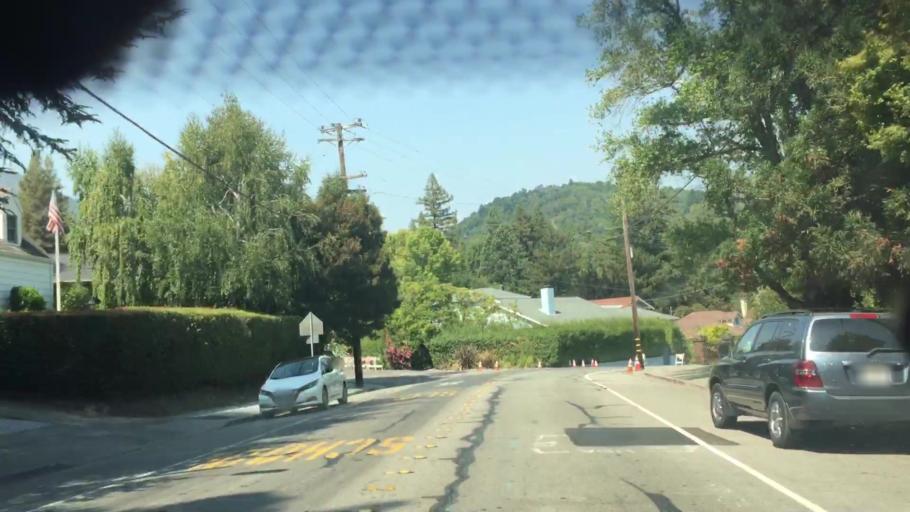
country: US
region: California
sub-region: Marin County
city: Larkspur
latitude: 37.9297
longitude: -122.5345
